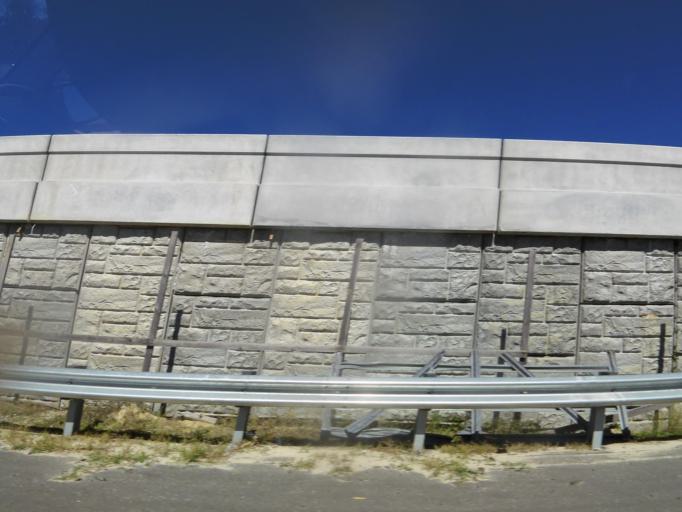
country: US
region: Florida
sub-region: Seminole County
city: Heathrow
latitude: 28.8152
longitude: -81.4247
